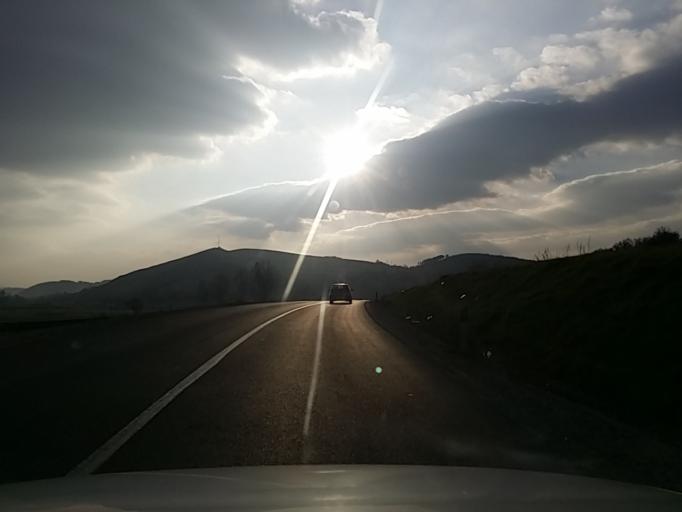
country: HU
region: Borsod-Abauj-Zemplen
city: Ozd
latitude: 48.2490
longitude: 20.3352
